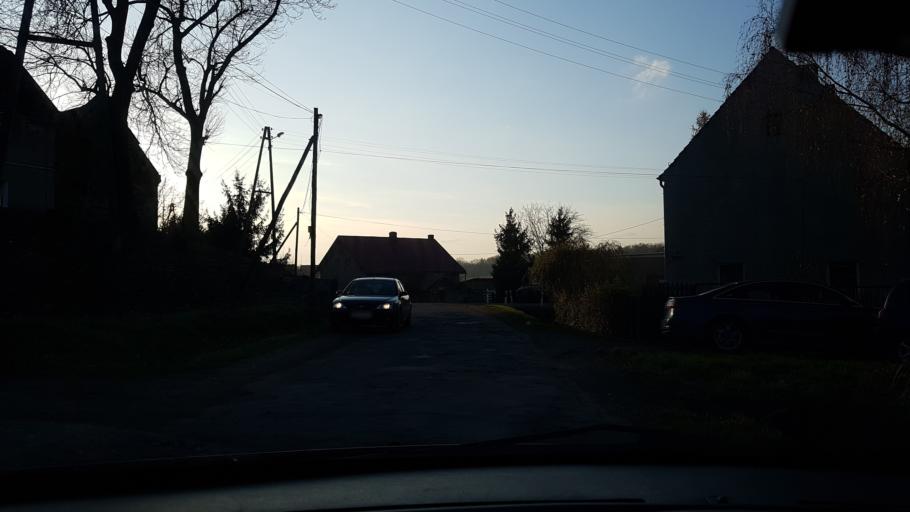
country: PL
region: Lower Silesian Voivodeship
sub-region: Powiat zabkowicki
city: Henrykow
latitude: 50.6584
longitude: 17.0762
